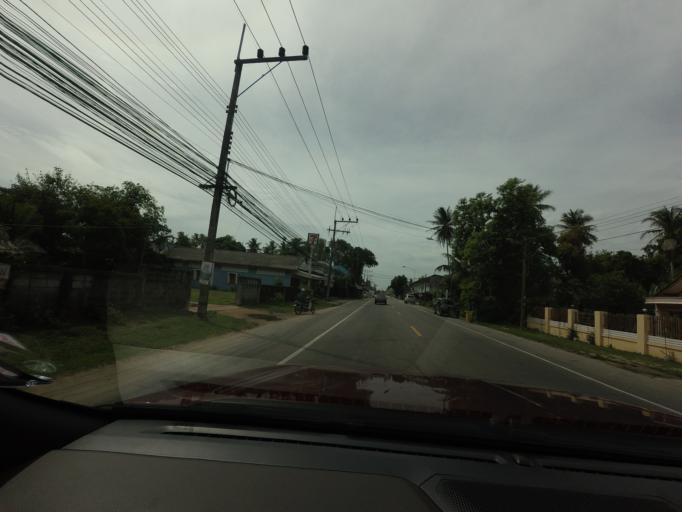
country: TH
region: Narathiwat
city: Tak Bai
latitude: 6.2402
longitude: 102.0802
